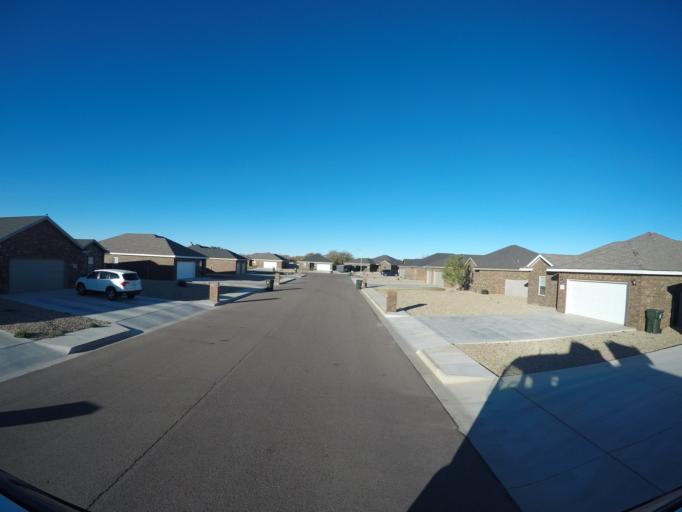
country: US
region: New Mexico
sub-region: Curry County
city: Clovis
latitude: 34.4090
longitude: -103.1723
